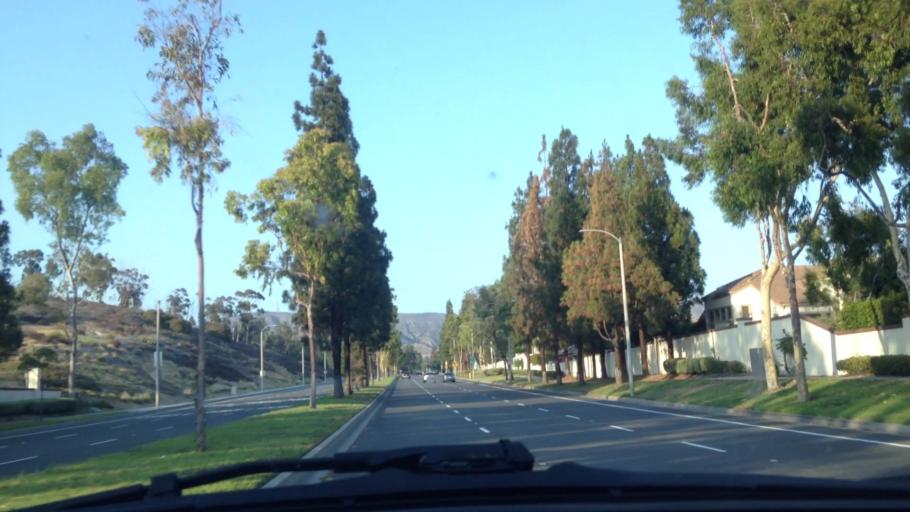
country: US
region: California
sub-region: Orange County
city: North Tustin
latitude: 33.7451
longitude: -117.7783
